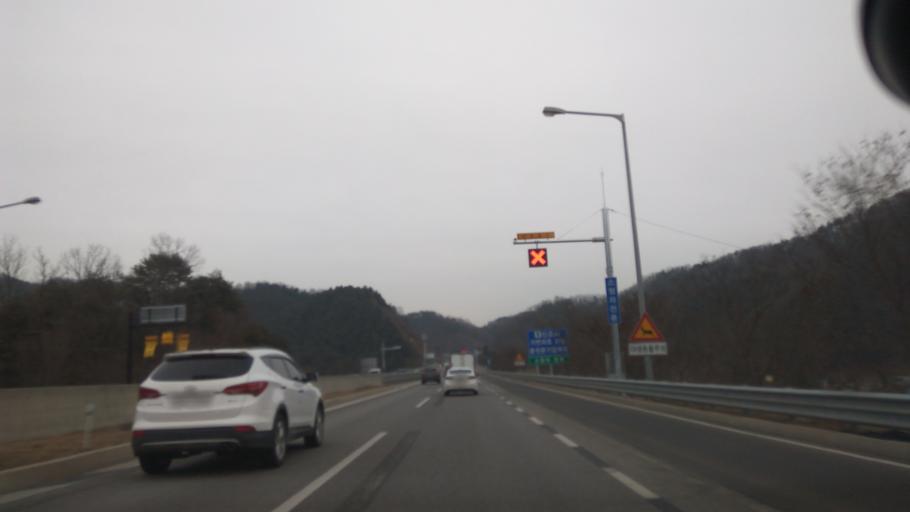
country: KR
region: Gangwon-do
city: Sindong
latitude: 37.7439
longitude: 127.6904
